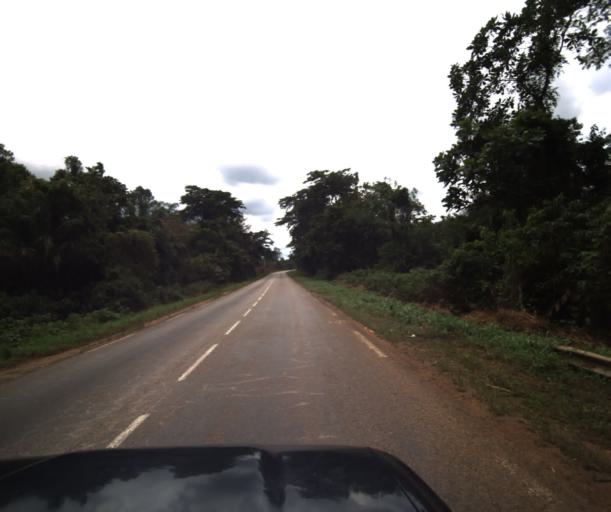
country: CM
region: Centre
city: Eseka
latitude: 3.8488
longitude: 10.4834
